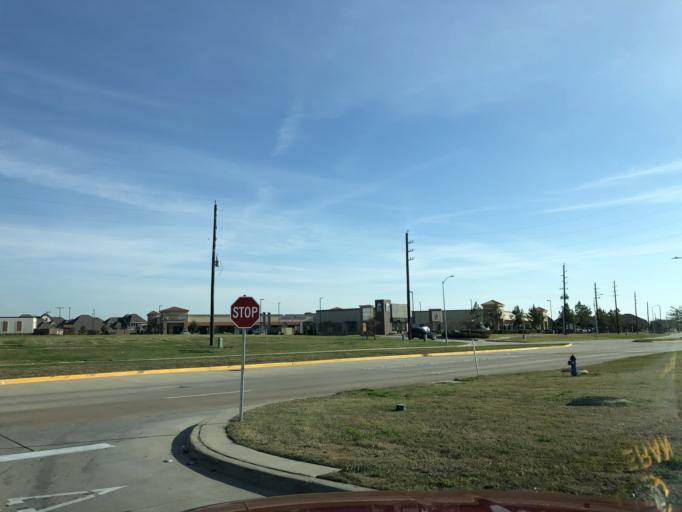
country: US
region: Texas
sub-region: Harris County
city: Tomball
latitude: 30.0555
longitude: -95.5753
